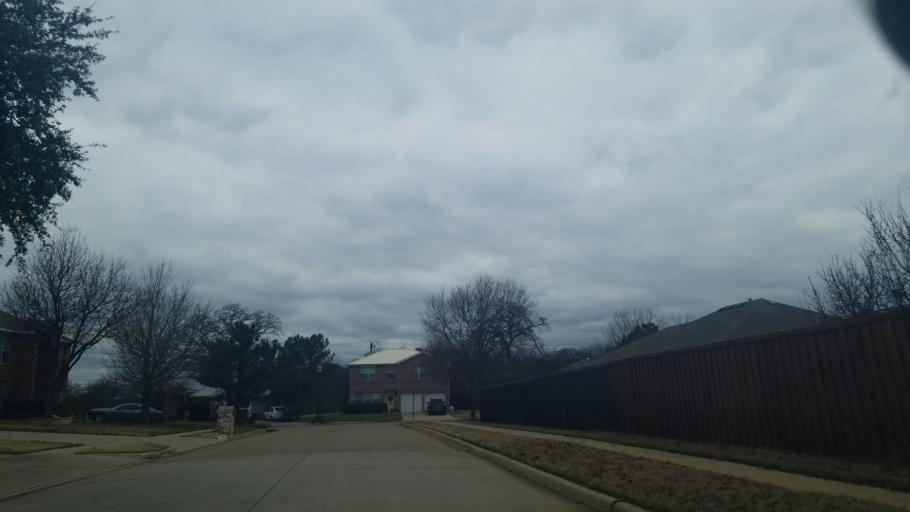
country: US
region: Texas
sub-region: Denton County
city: Corinth
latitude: 33.1326
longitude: -97.0883
